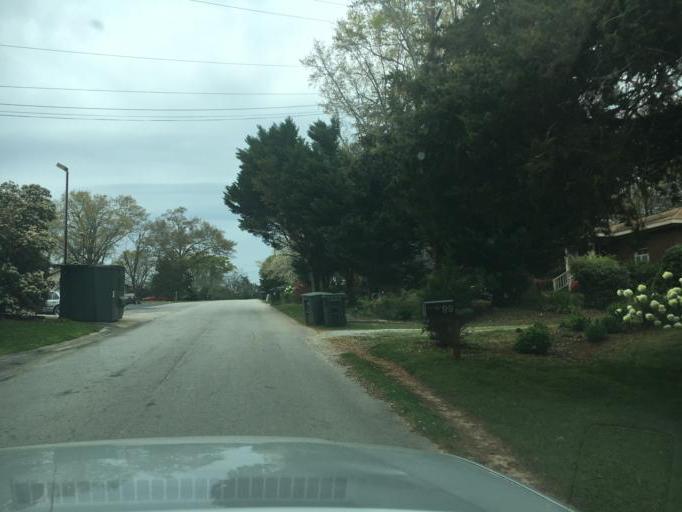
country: US
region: Georgia
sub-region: Stephens County
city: Toccoa
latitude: 34.5747
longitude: -83.3115
